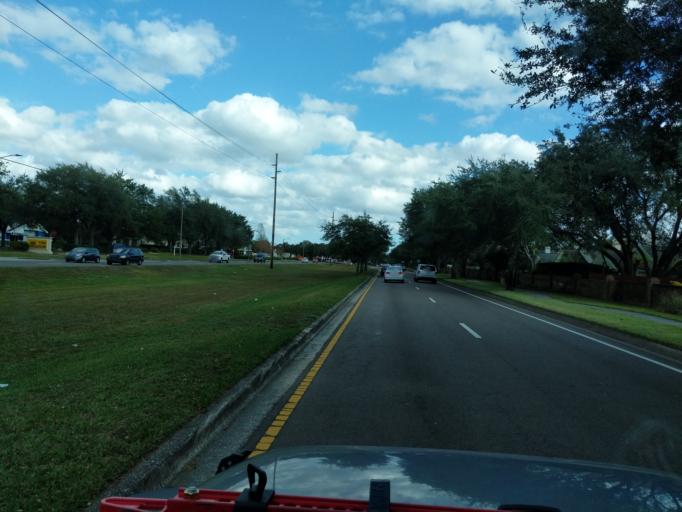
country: US
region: Florida
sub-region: Seminole County
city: Oviedo
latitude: 28.6559
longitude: -81.1834
